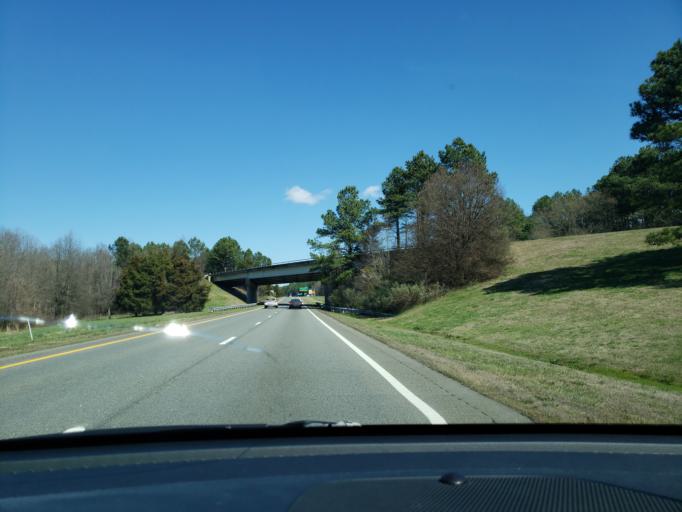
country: US
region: North Carolina
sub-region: Wake County
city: Morrisville
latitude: 35.9027
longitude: -78.8729
